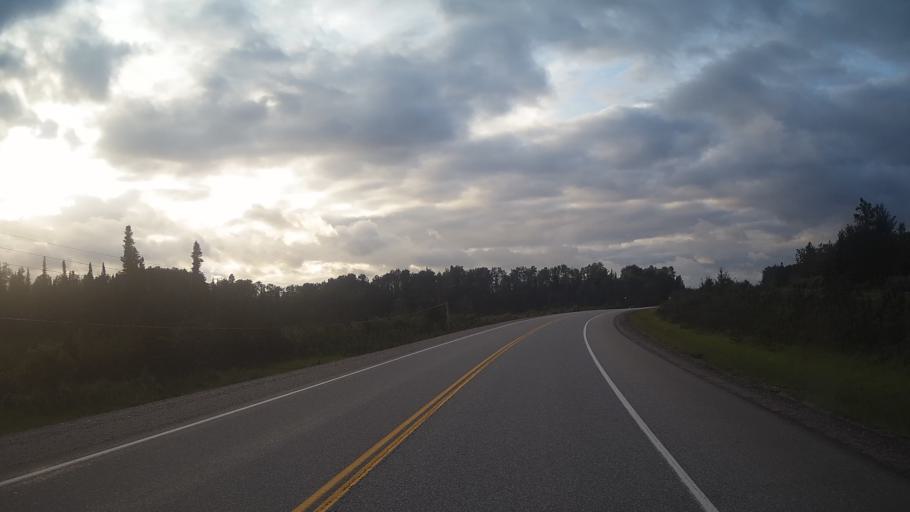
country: CA
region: Ontario
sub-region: Rainy River District
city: Atikokan
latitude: 49.0330
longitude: -90.4632
